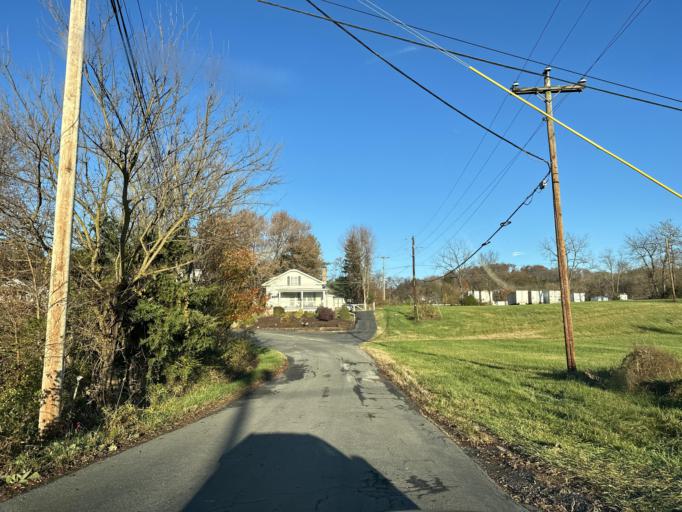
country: US
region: Virginia
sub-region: Augusta County
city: Weyers Cave
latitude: 38.2885
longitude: -78.9140
